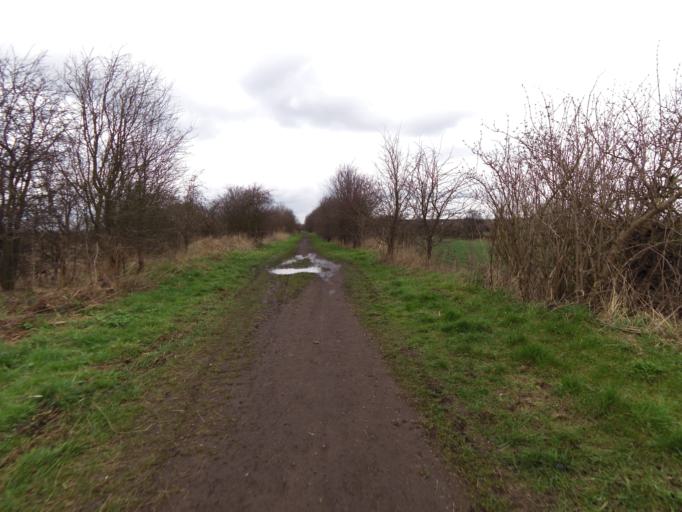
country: GB
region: England
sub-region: Doncaster
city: Bentley
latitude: 53.5524
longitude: -1.1555
